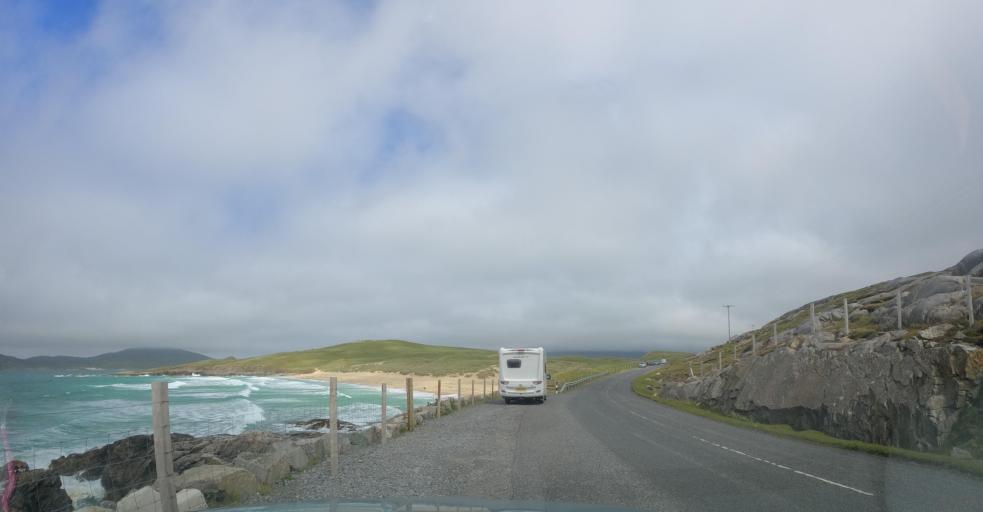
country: GB
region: Scotland
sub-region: Eilean Siar
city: Harris
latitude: 57.8595
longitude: -6.9936
